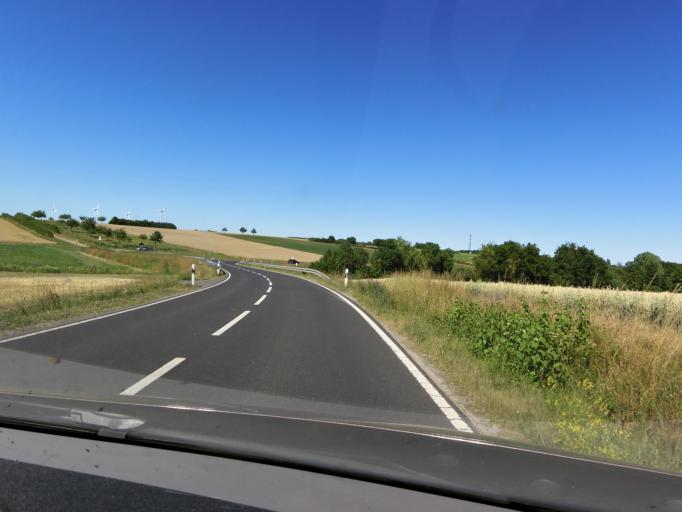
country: DE
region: Bavaria
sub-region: Regierungsbezirk Unterfranken
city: Biebelried
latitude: 49.7330
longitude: 10.0934
